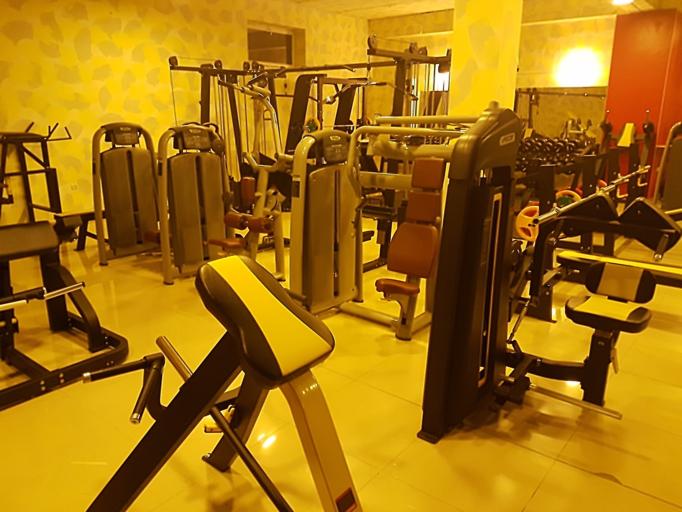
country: AM
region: Ararat
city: Masis
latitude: 40.0611
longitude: 44.4472
